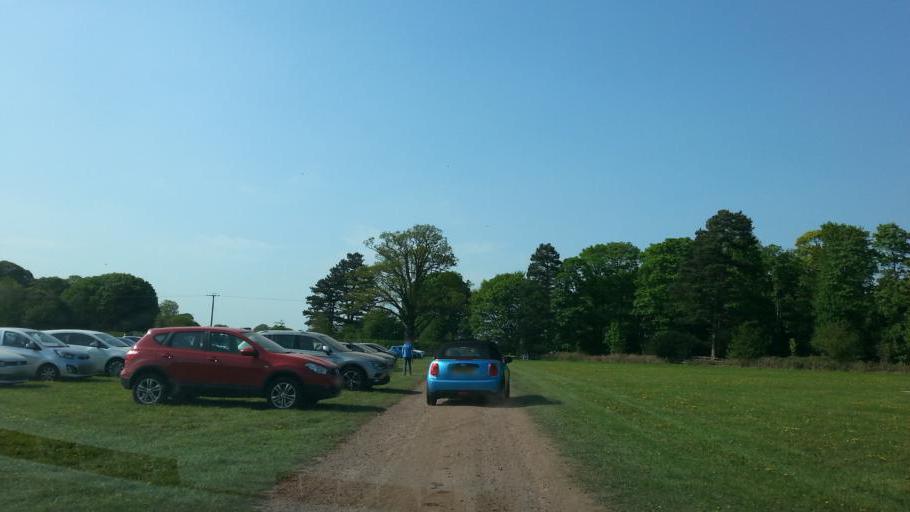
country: GB
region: England
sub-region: Nottinghamshire
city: Worksop
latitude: 53.2689
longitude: -1.0590
